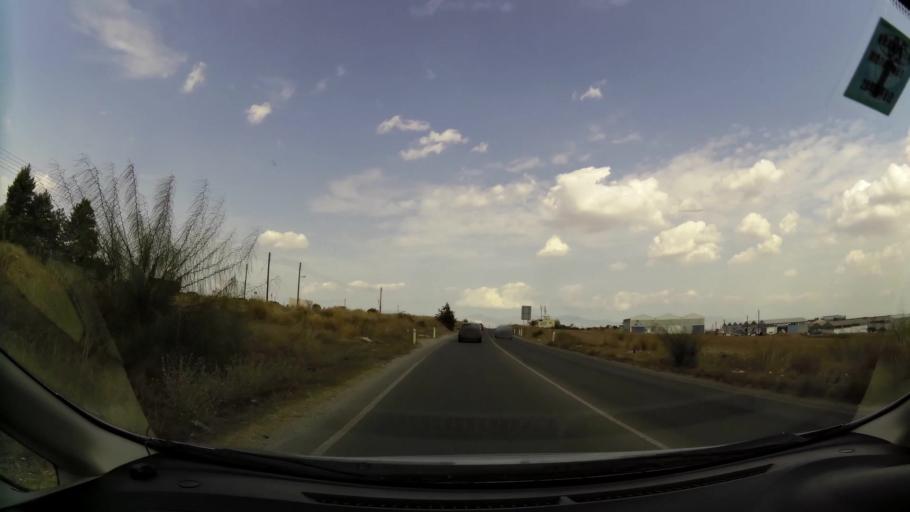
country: CY
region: Lefkosia
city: Tseri
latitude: 35.0989
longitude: 33.3272
